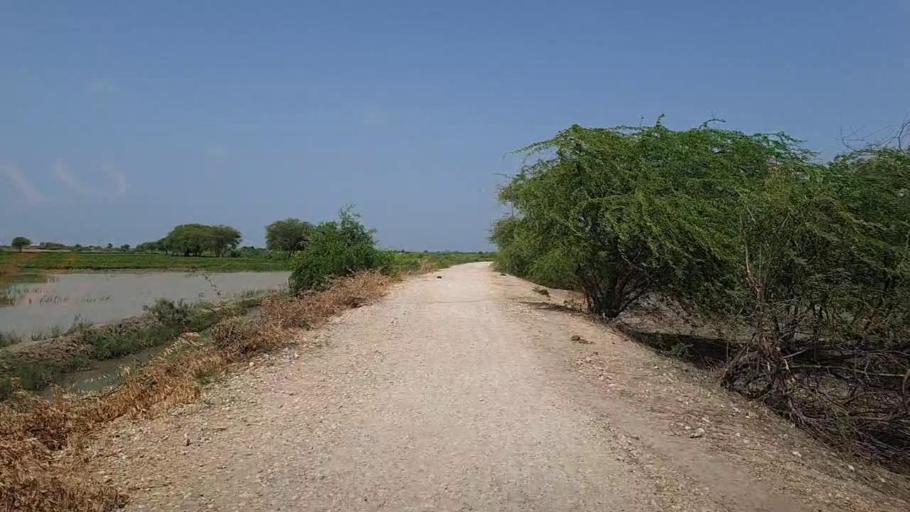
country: PK
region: Sindh
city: Mirpur Batoro
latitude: 24.6483
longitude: 68.4273
